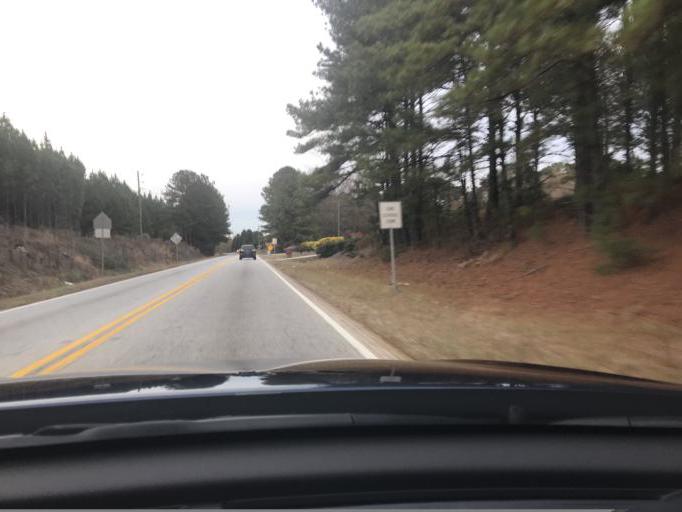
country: US
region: Georgia
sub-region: Newton County
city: Porterdale
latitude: 33.5999
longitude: -83.9161
